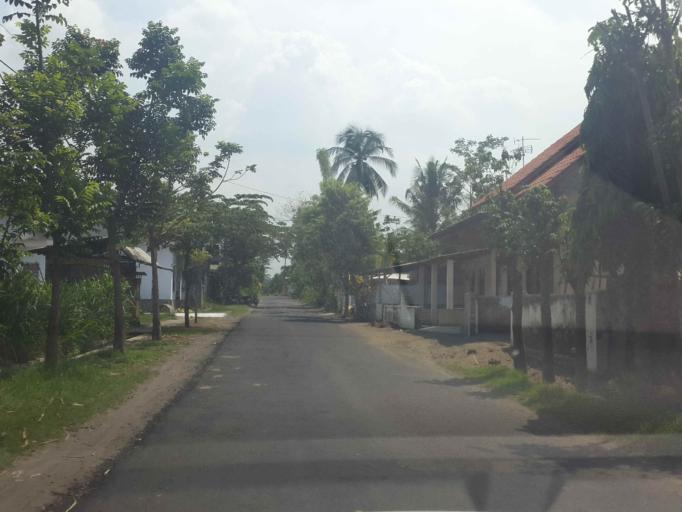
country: ID
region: East Java
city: Kediri
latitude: -7.8933
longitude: 112.0147
